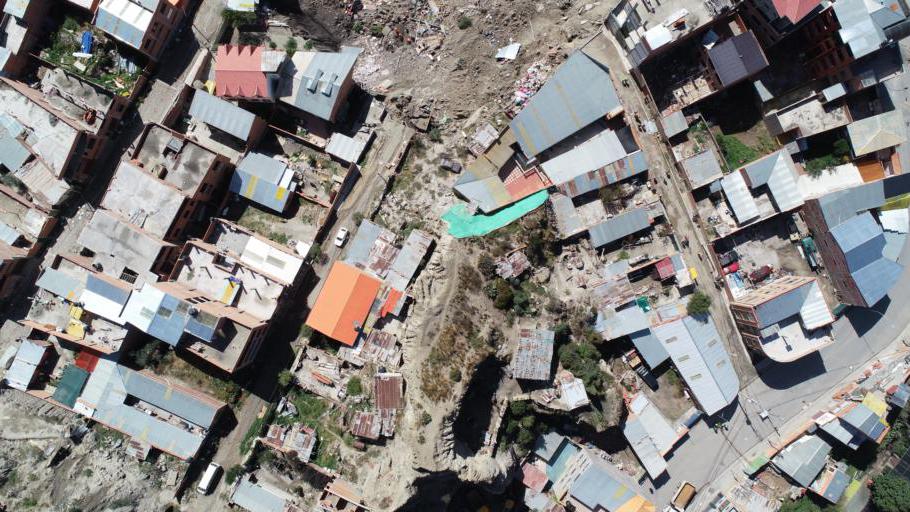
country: BO
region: La Paz
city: La Paz
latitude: -16.5192
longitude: -68.1242
